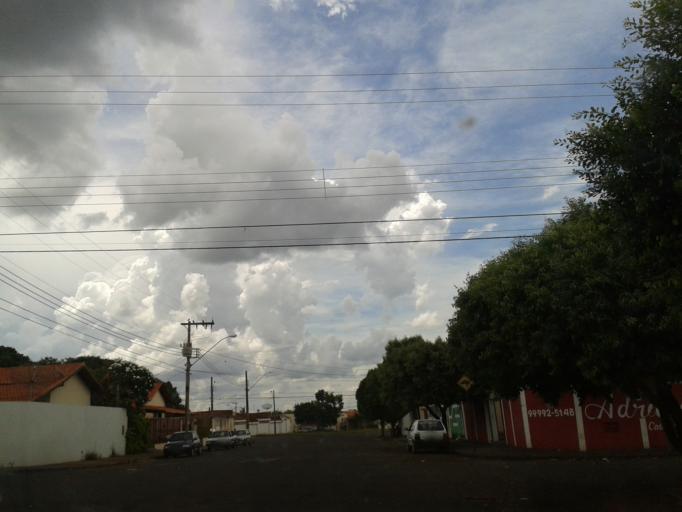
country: BR
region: Minas Gerais
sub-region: Ituiutaba
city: Ituiutaba
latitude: -18.9848
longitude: -49.4546
